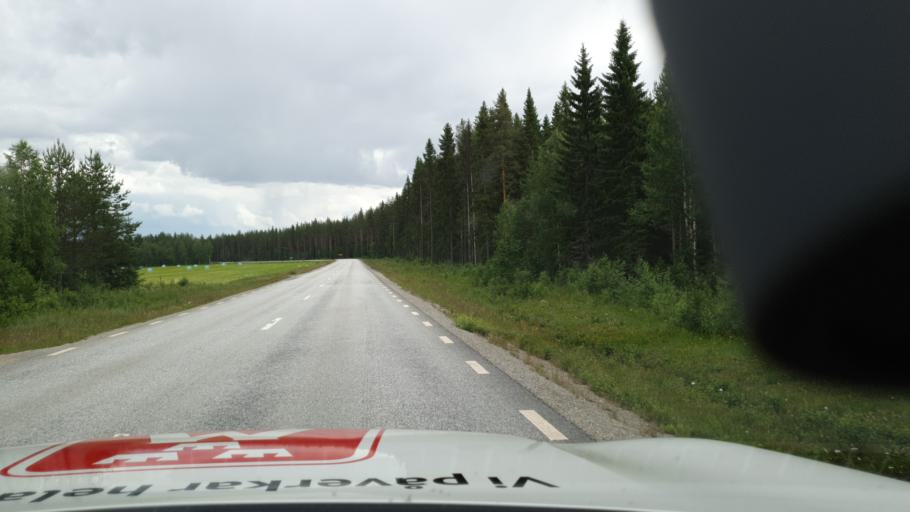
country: SE
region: Vaesterbotten
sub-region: Vindelns Kommun
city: Vindeln
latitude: 64.0952
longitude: 19.6083
